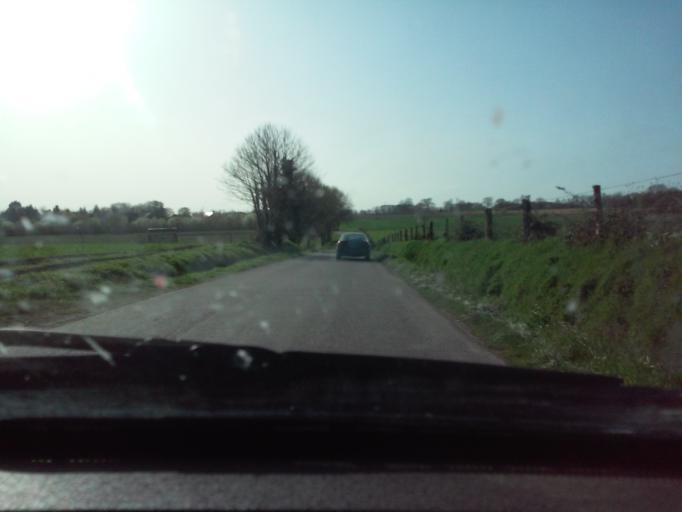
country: FR
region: Brittany
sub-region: Departement d'Ille-et-Vilaine
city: Saint-Jean-sur-Couesnon
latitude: 48.3008
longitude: -1.3262
